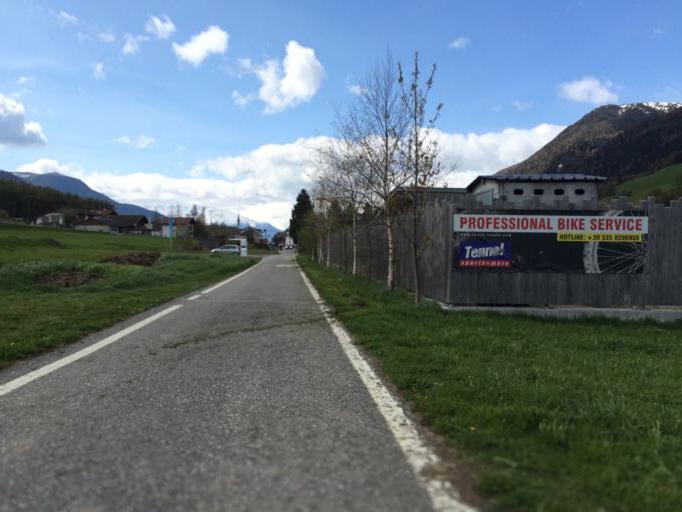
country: IT
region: Trentino-Alto Adige
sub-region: Bolzano
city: Curon Venosta
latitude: 46.7705
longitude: 10.5325
